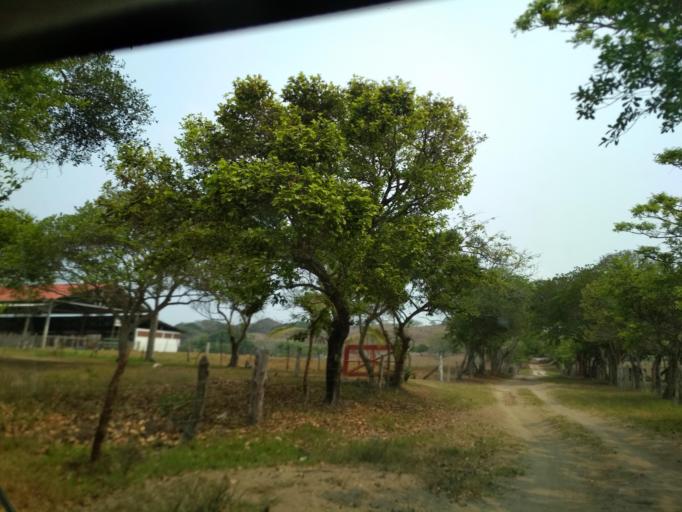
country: MX
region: Veracruz
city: Anton Lizardo
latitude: 19.0161
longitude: -95.9886
